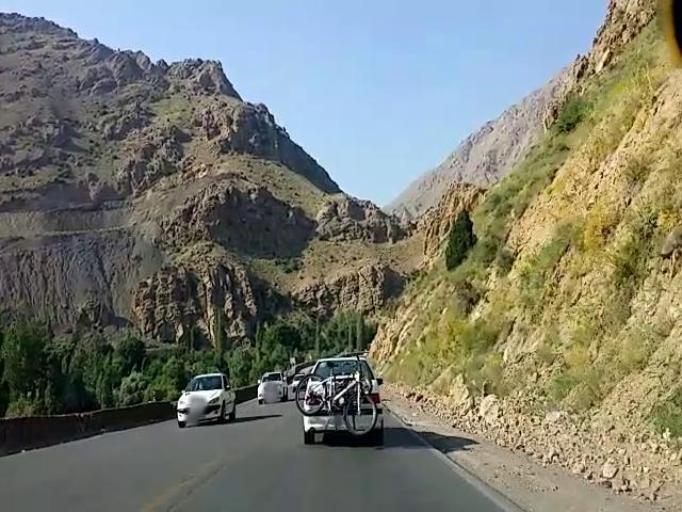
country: IR
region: Tehran
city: Tajrish
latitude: 36.0720
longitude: 51.3098
